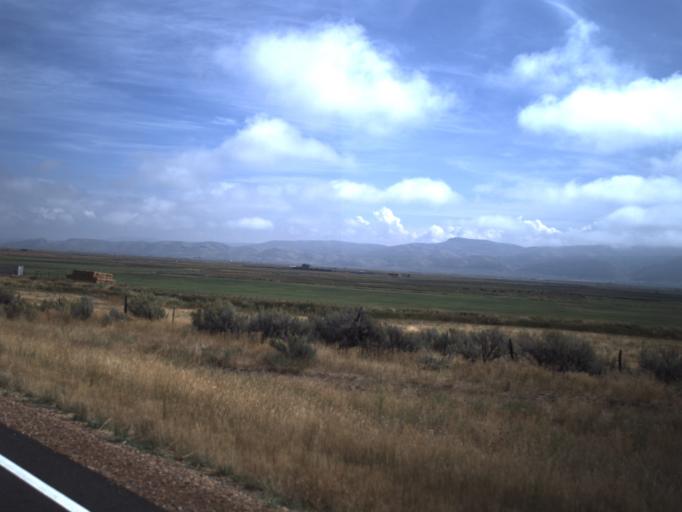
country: US
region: Utah
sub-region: Rich County
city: Randolph
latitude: 41.7007
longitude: -111.1622
